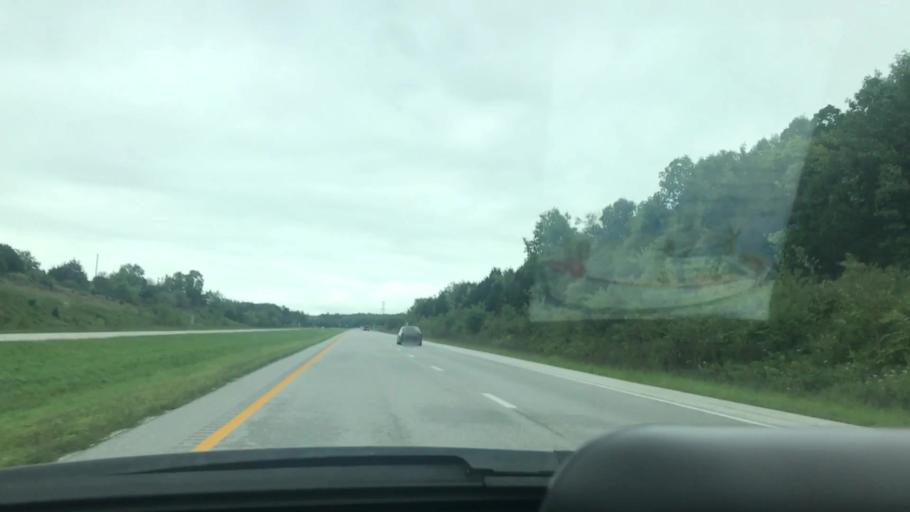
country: US
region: Missouri
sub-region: Greene County
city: Strafford
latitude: 37.3130
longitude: -93.1714
